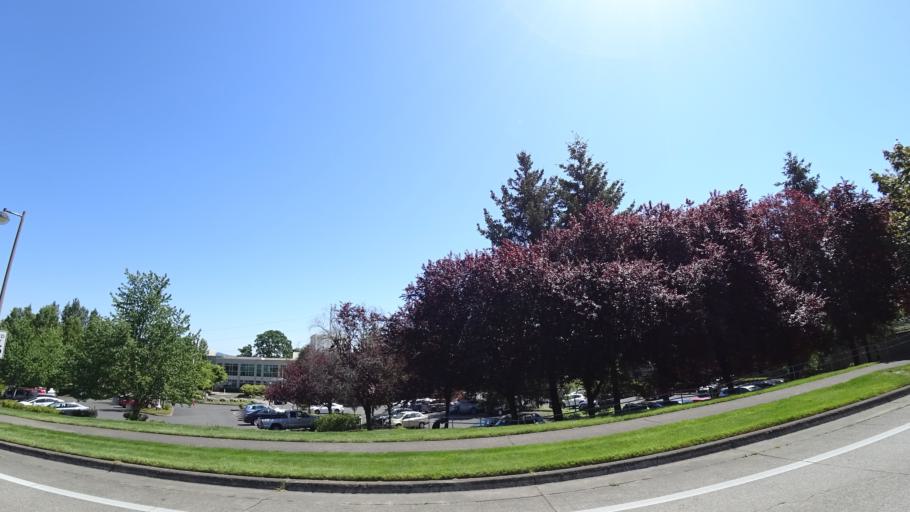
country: US
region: Oregon
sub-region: Washington County
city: Aloha
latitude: 45.4923
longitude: -122.8418
